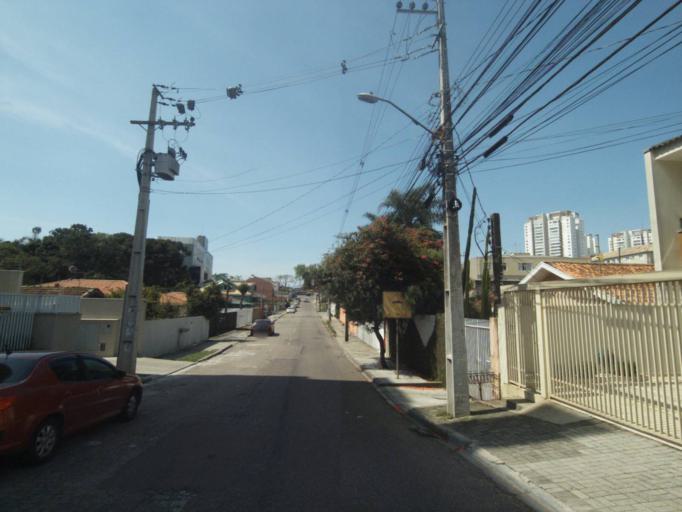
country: BR
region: Parana
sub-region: Curitiba
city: Curitiba
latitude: -25.4696
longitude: -49.2988
